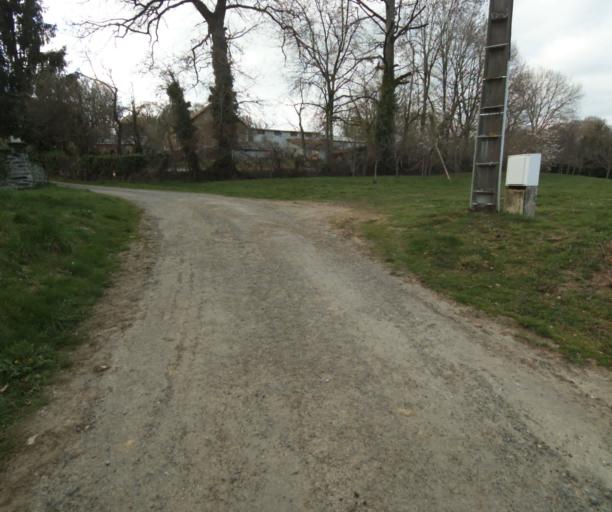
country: FR
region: Limousin
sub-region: Departement de la Correze
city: Saint-Clement
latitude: 45.3605
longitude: 1.6468
